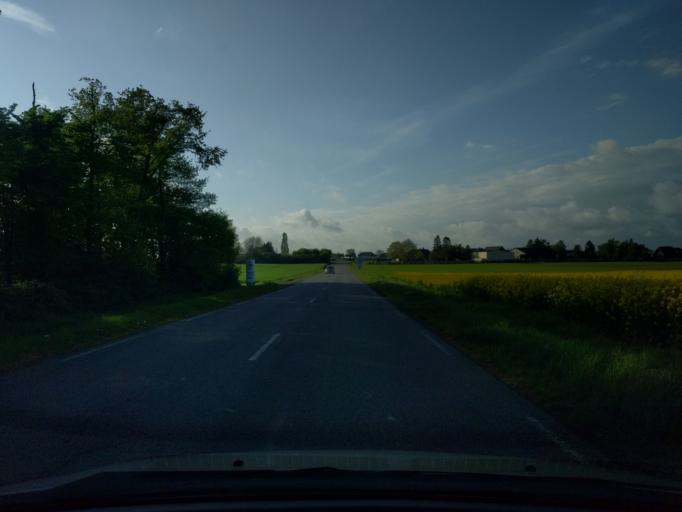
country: FR
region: Haute-Normandie
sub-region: Departement de l'Eure
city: Damville
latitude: 48.9047
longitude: 1.0263
